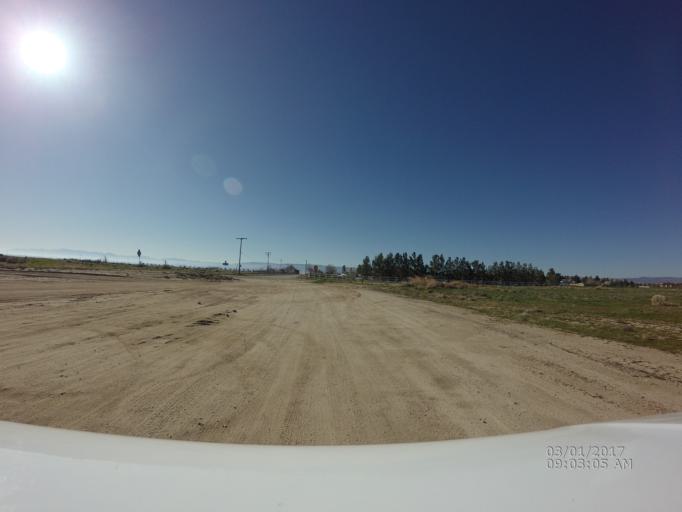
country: US
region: California
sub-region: Kern County
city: Rosamond
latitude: 34.7770
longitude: -118.2728
